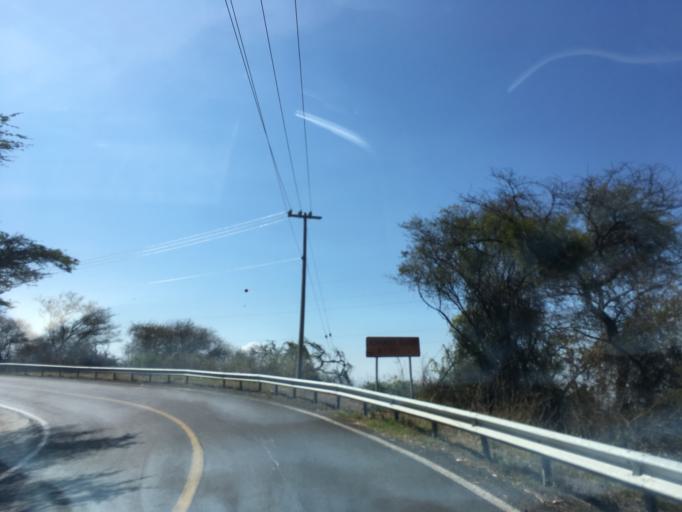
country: MX
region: Michoacan
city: Tzitzio
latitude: 19.6487
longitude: -100.9893
